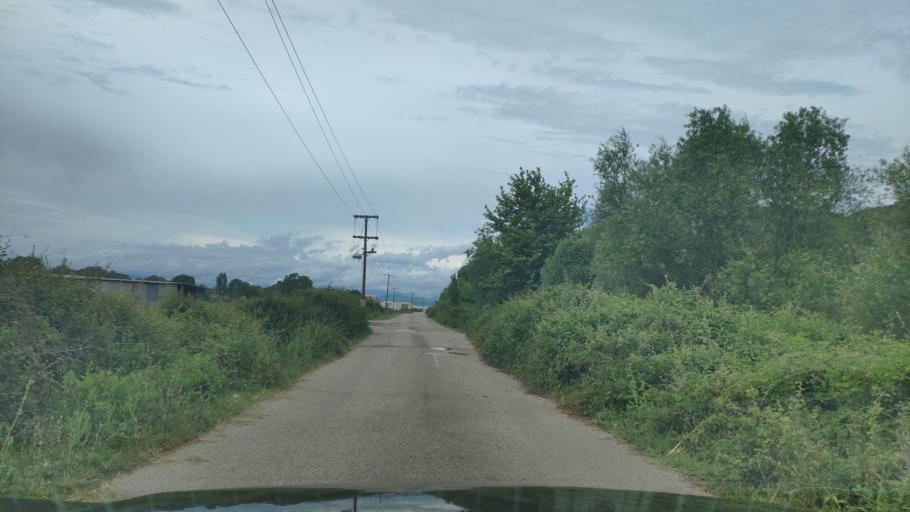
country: GR
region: West Greece
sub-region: Nomos Aitolias kai Akarnanias
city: Vonitsa
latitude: 38.9136
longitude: 20.9081
